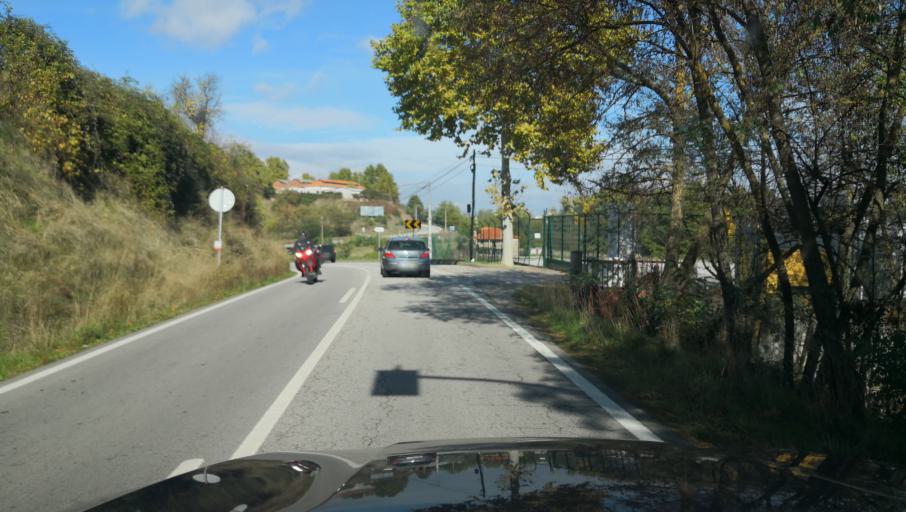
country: PT
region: Vila Real
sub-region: Chaves
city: Chaves
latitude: 41.7284
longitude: -7.4785
